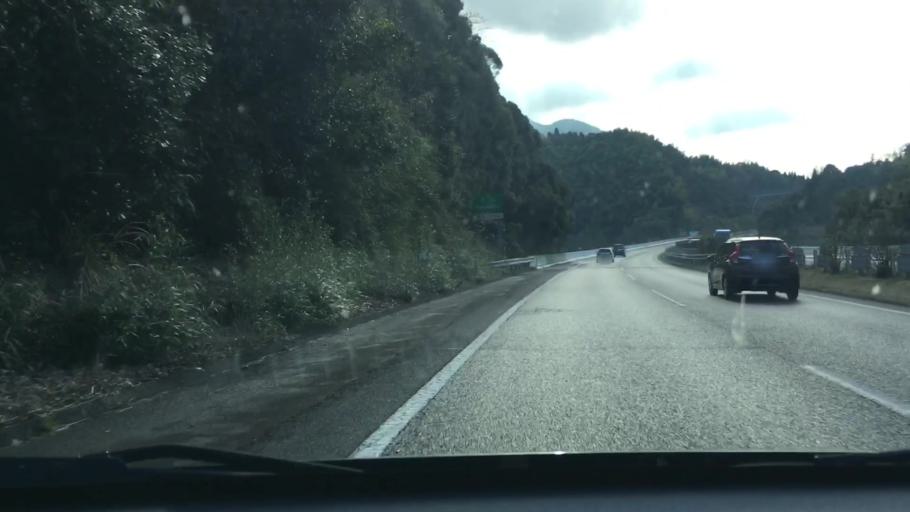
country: JP
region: Kumamoto
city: Matsubase
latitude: 32.5516
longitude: 130.6934
